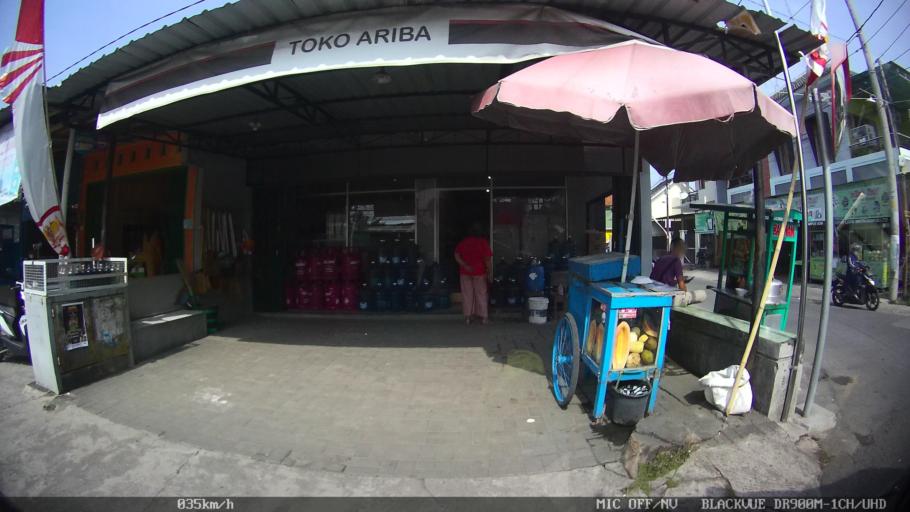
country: ID
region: Daerah Istimewa Yogyakarta
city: Depok
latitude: -7.7687
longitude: 110.4245
